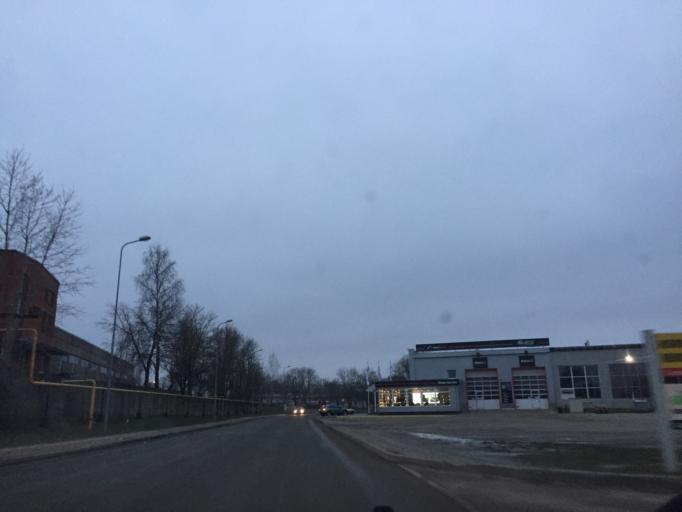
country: LV
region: Cesu Rajons
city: Cesis
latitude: 57.3111
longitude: 25.2861
